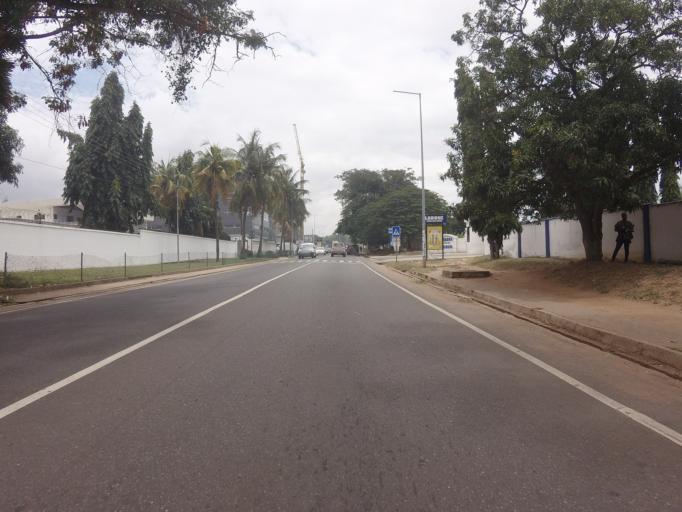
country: GH
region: Greater Accra
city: Accra
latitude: 5.5648
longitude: -0.1714
